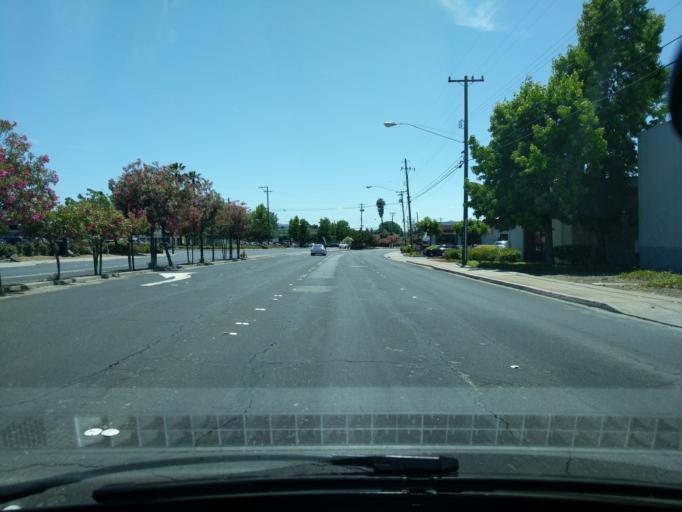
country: US
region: California
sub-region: Contra Costa County
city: Concord
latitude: 37.9620
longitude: -122.0322
